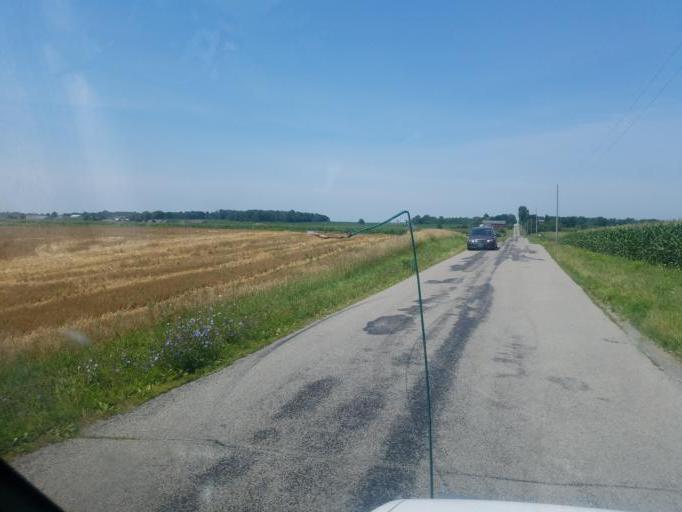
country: US
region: Ohio
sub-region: Logan County
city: West Liberty
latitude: 40.2890
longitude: -83.7767
